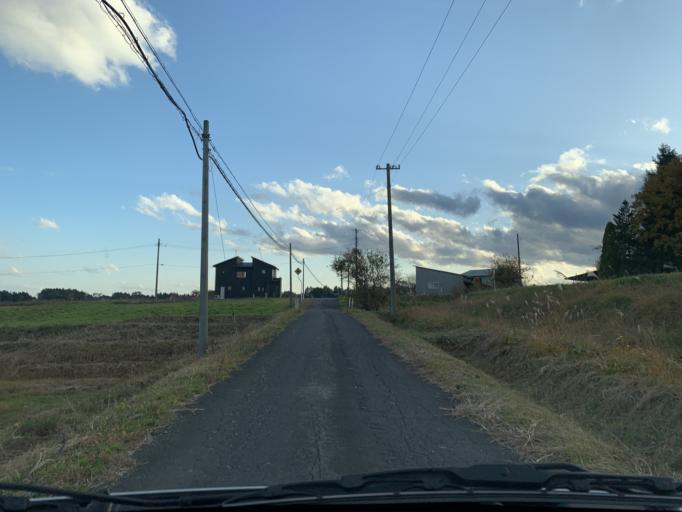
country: JP
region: Iwate
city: Mizusawa
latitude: 39.1025
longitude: 141.0395
